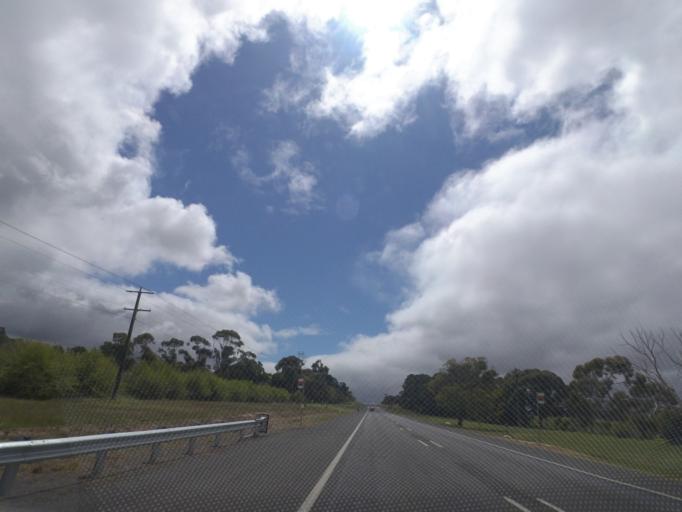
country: AU
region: Victoria
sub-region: Ballarat North
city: Lake Wendouree
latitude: -37.5026
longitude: 143.8456
